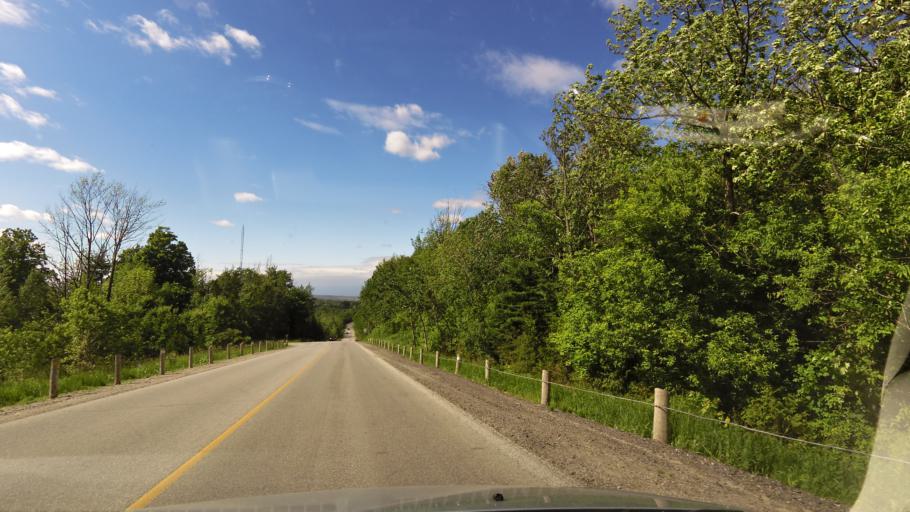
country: CA
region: Ontario
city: Bradford West Gwillimbury
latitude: 44.1664
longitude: -79.6167
